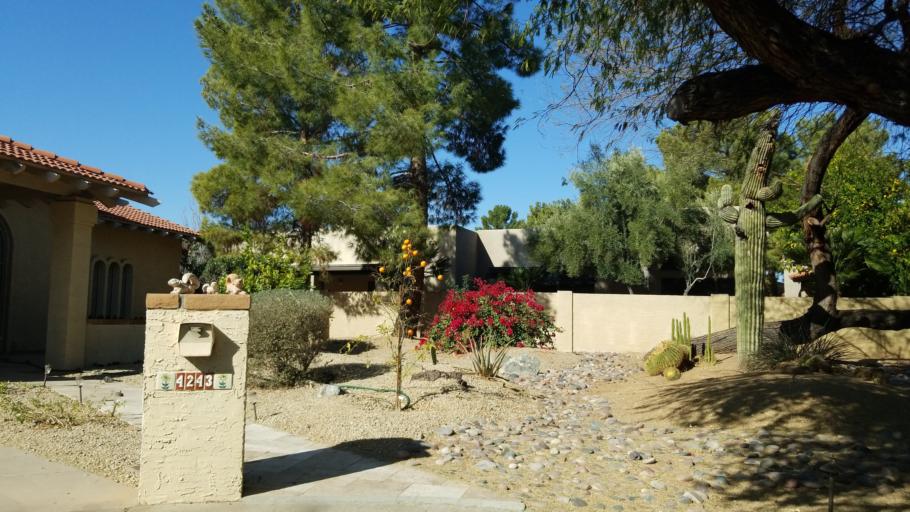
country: US
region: Arizona
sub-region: Maricopa County
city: Paradise Valley
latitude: 33.5927
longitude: -111.9881
